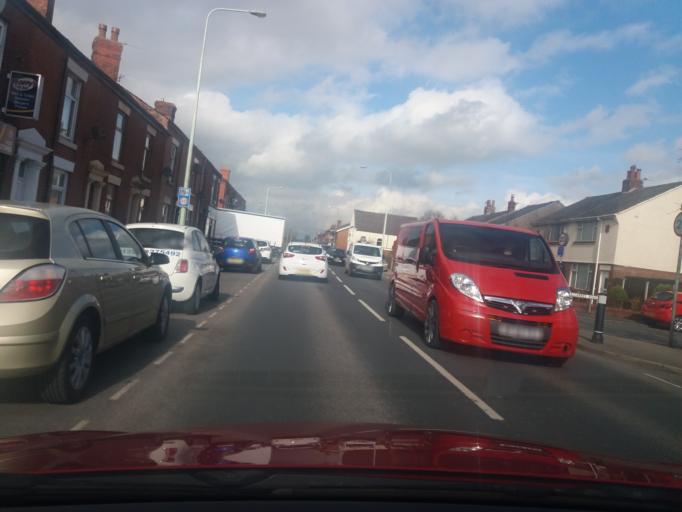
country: GB
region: England
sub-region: Lancashire
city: Chorley
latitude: 53.6425
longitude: -2.6385
